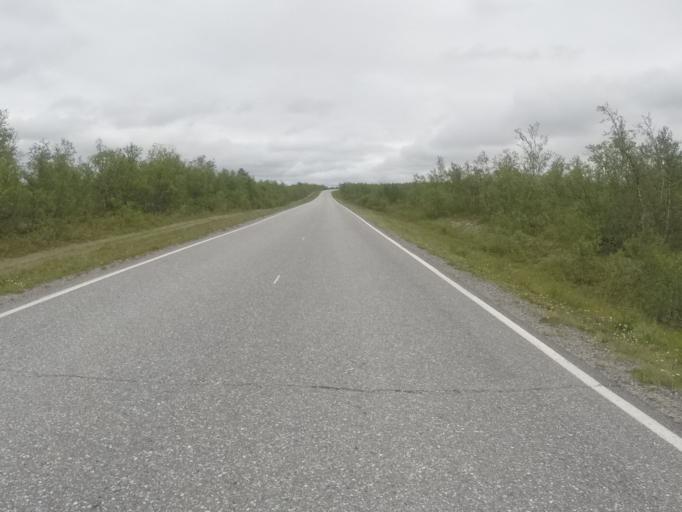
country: NO
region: Finnmark Fylke
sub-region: Kautokeino
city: Kautokeino
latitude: 69.0570
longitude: 23.1287
